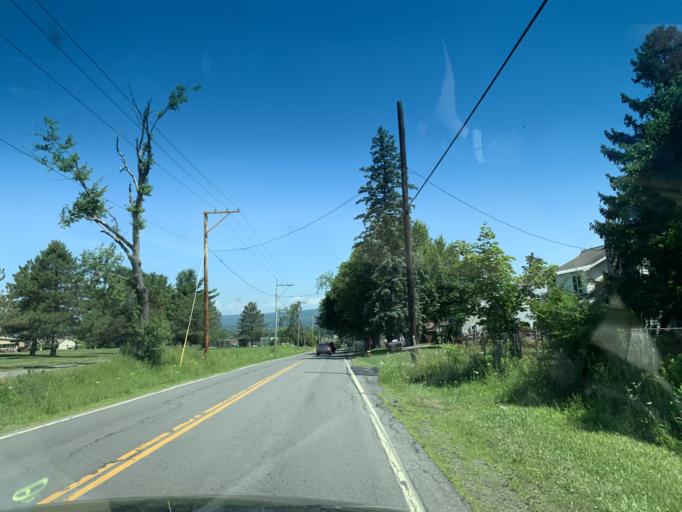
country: US
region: New York
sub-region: Oneida County
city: Utica
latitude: 43.0775
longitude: -75.2347
